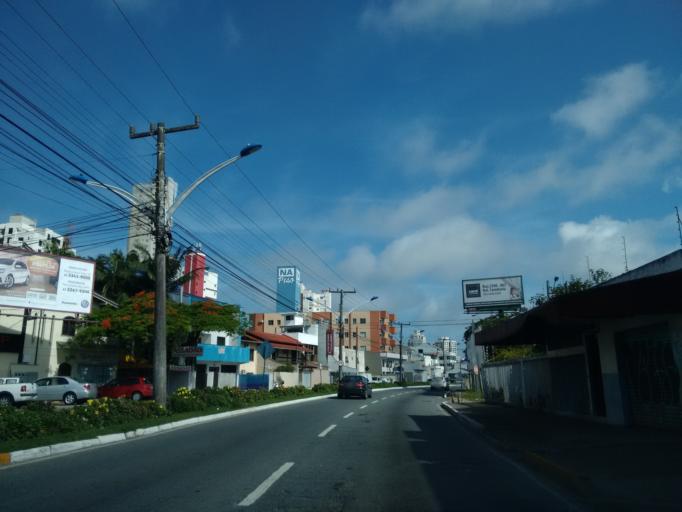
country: BR
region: Santa Catarina
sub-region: Itajai
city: Itajai
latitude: -26.9148
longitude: -48.6567
